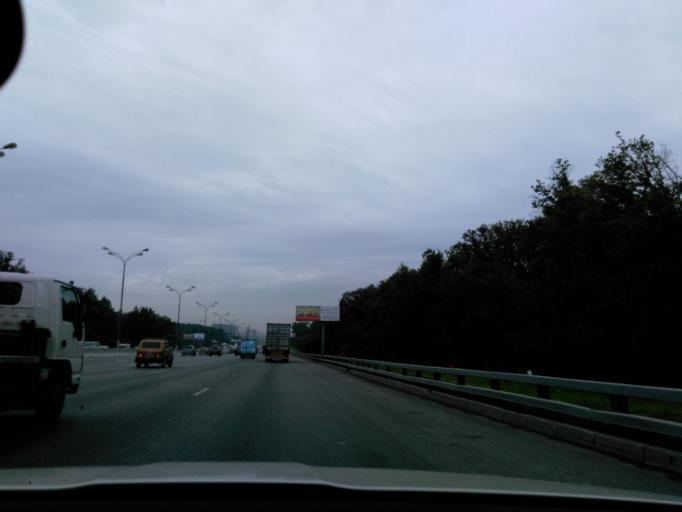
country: RU
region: Moscow
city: Vostochnyy
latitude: 55.7985
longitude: 37.8401
